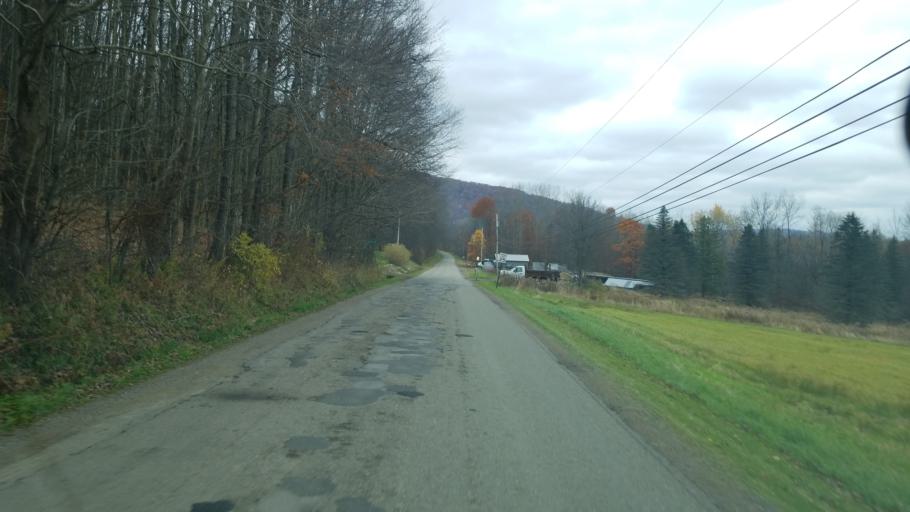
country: US
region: Pennsylvania
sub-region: McKean County
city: Smethport
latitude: 41.7984
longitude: -78.4303
